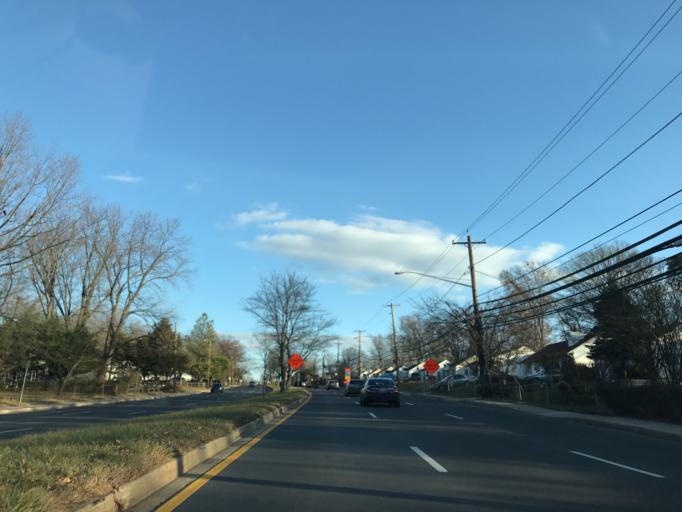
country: US
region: Maryland
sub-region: Montgomery County
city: Glenmont
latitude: 39.0592
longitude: -77.0588
